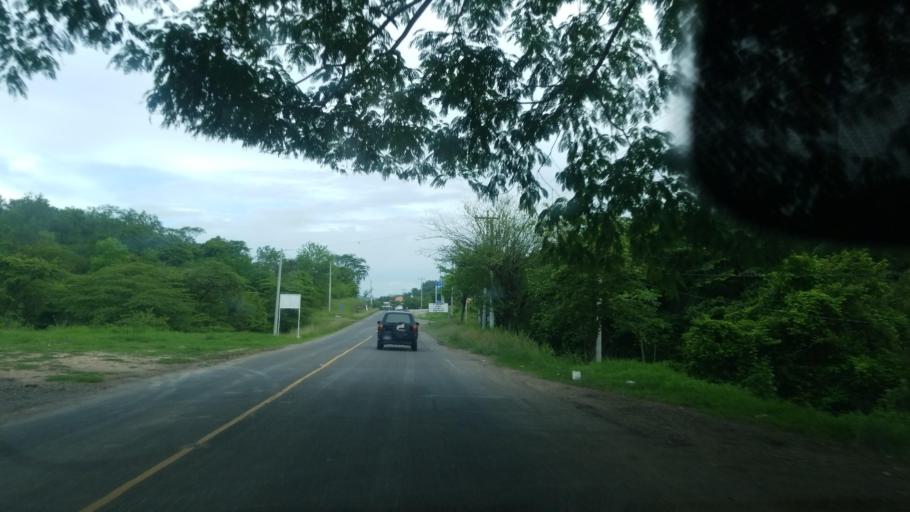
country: HN
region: Santa Barbara
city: Santa Barbara
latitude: 14.9059
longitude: -88.2530
